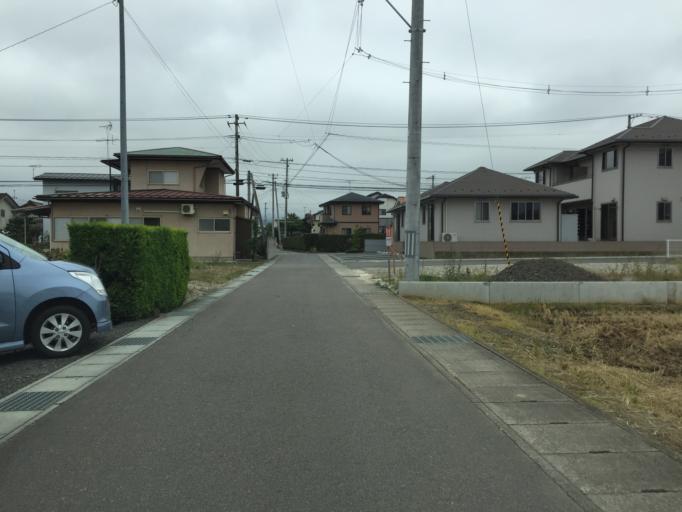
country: JP
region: Fukushima
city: Fukushima-shi
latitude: 37.7419
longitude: 140.4417
